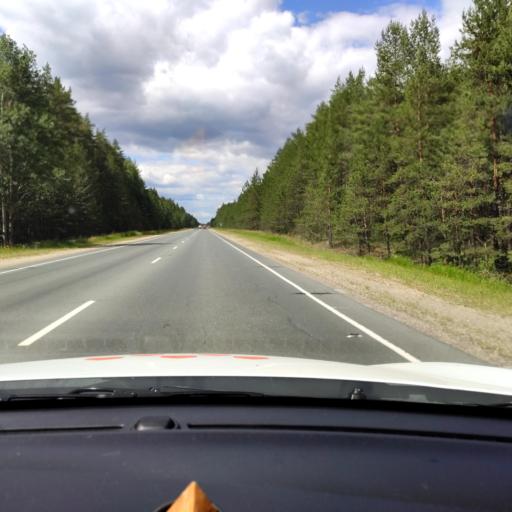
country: RU
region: Mariy-El
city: Krasnogorskiy
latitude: 56.0653
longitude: 48.3671
